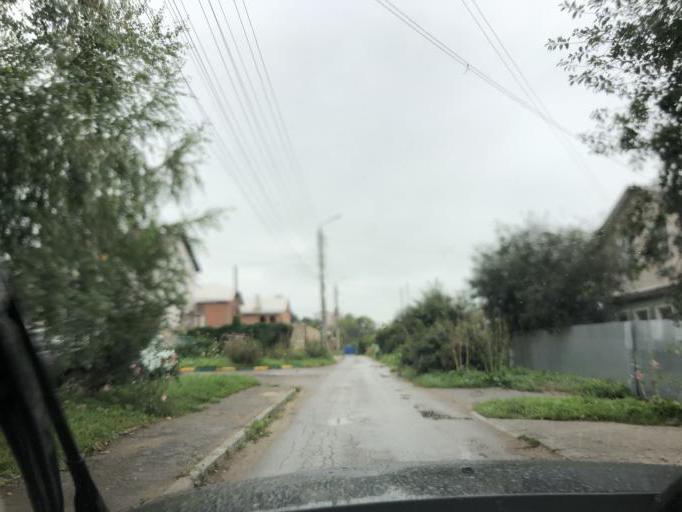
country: RU
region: Tula
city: Tula
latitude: 54.2027
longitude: 37.5398
